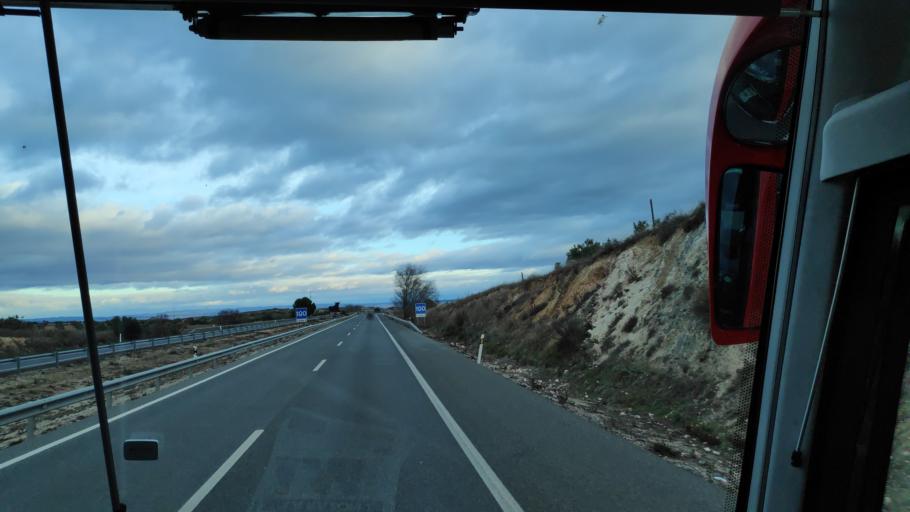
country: ES
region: Madrid
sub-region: Provincia de Madrid
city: Villarejo de Salvanes
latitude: 40.1514
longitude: -3.2394
